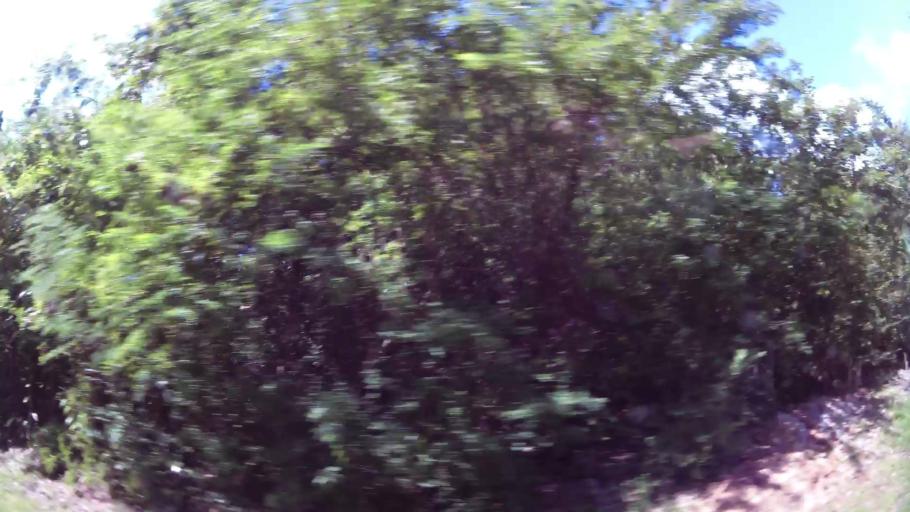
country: DM
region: Saint John
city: Portsmouth
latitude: 15.5918
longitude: -61.4636
